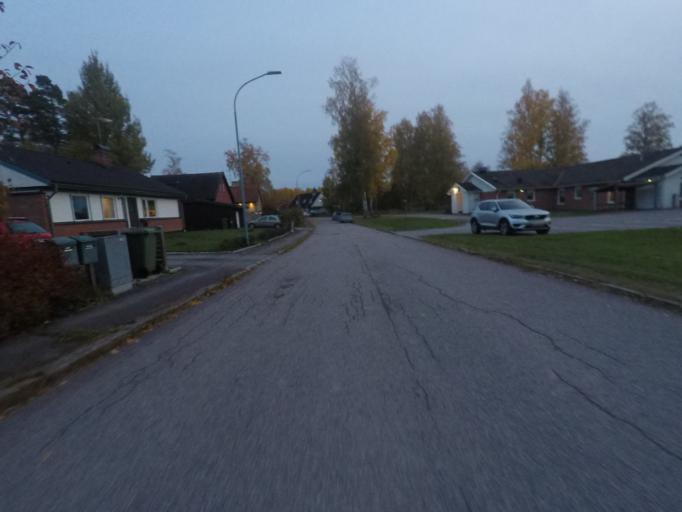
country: SE
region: OErebro
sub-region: Karlskoga Kommun
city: Karlskoga
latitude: 59.3081
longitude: 14.5013
